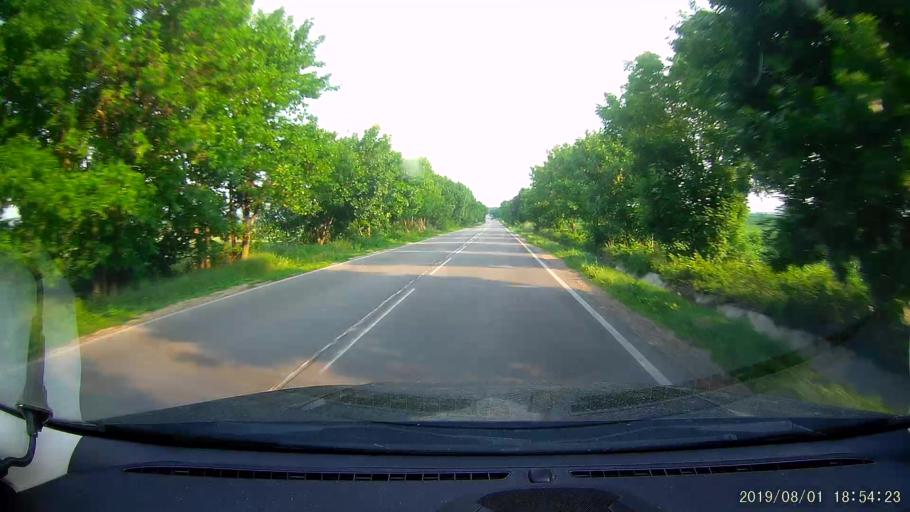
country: BG
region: Shumen
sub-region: Obshtina Shumen
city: Shumen
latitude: 43.1999
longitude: 27.0016
